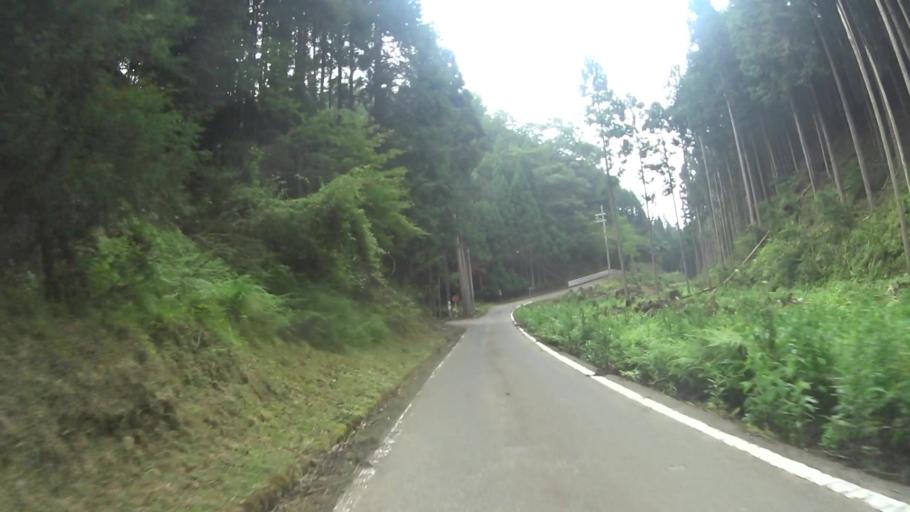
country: JP
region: Kyoto
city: Kameoka
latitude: 35.1650
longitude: 135.5647
